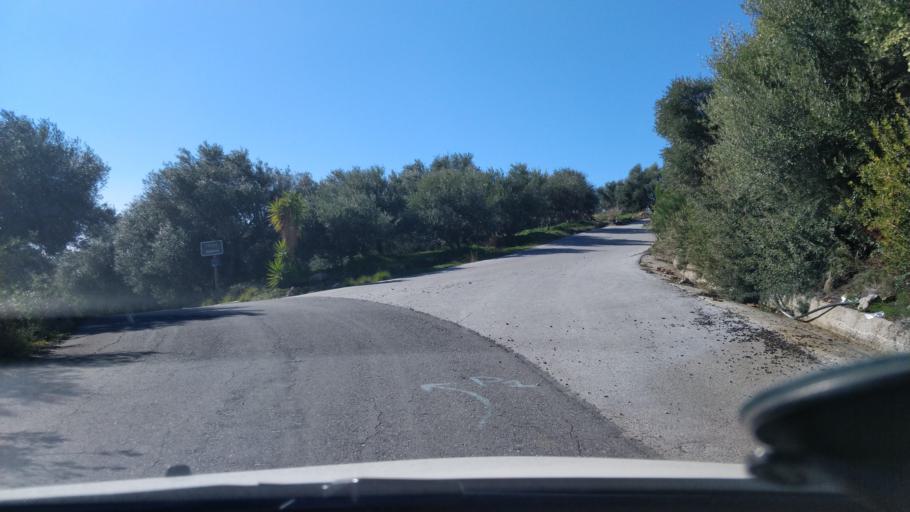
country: GR
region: Crete
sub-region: Nomos Lasithiou
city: Gra Liyia
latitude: 35.0190
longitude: 25.5532
